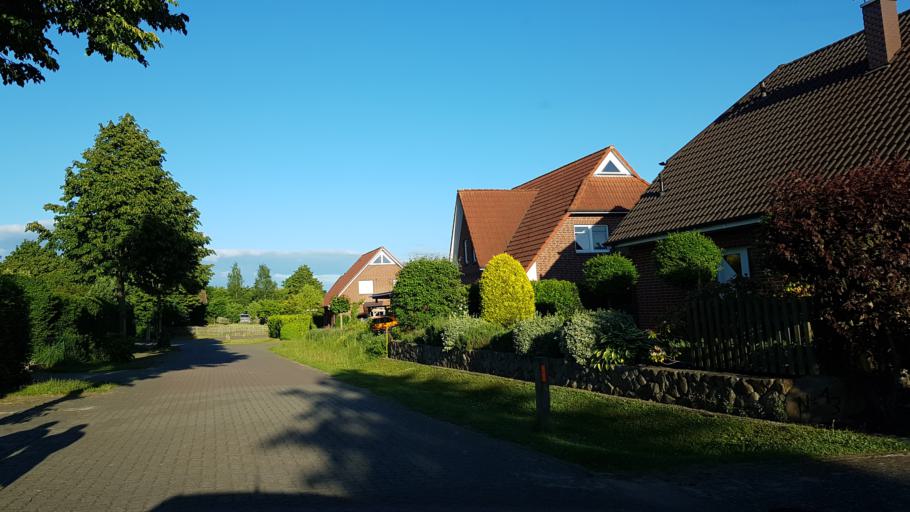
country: DE
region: Lower Saxony
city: Wulfsen
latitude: 53.3074
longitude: 10.1482
